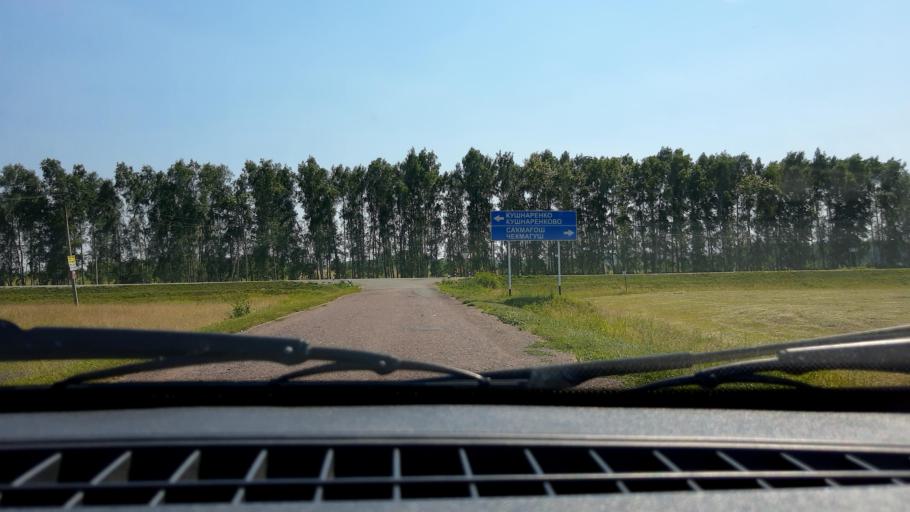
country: RU
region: Bashkortostan
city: Kushnarenkovo
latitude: 55.0586
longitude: 55.1625
